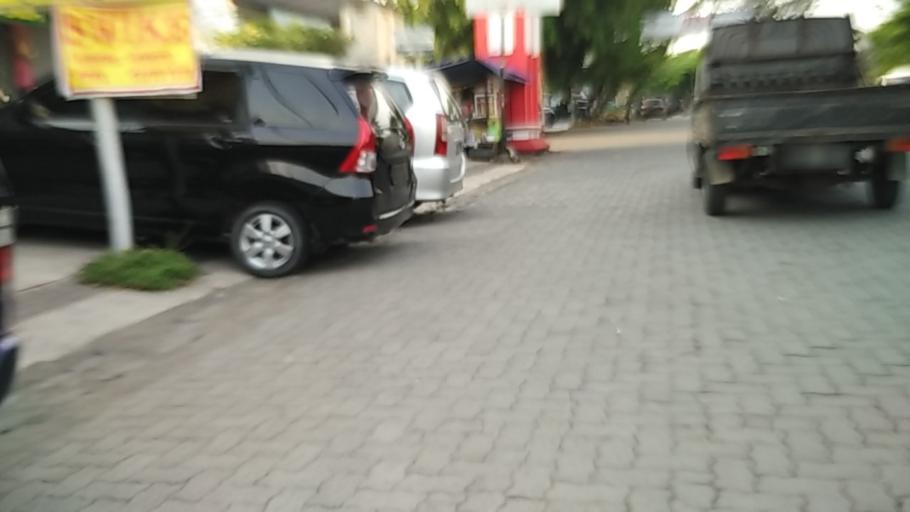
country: ID
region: Central Java
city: Semarang
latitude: -6.9754
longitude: 110.3906
